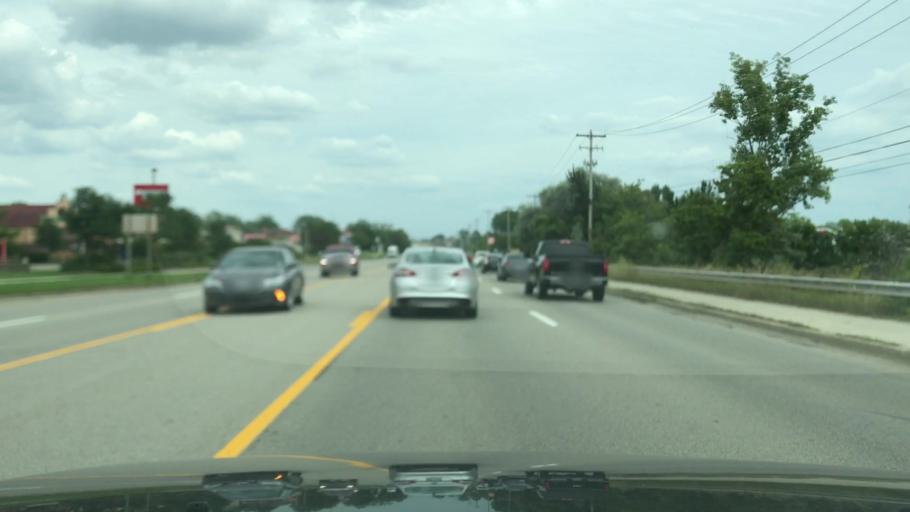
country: US
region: Michigan
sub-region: Kent County
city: East Grand Rapids
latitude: 42.9125
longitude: -85.5574
